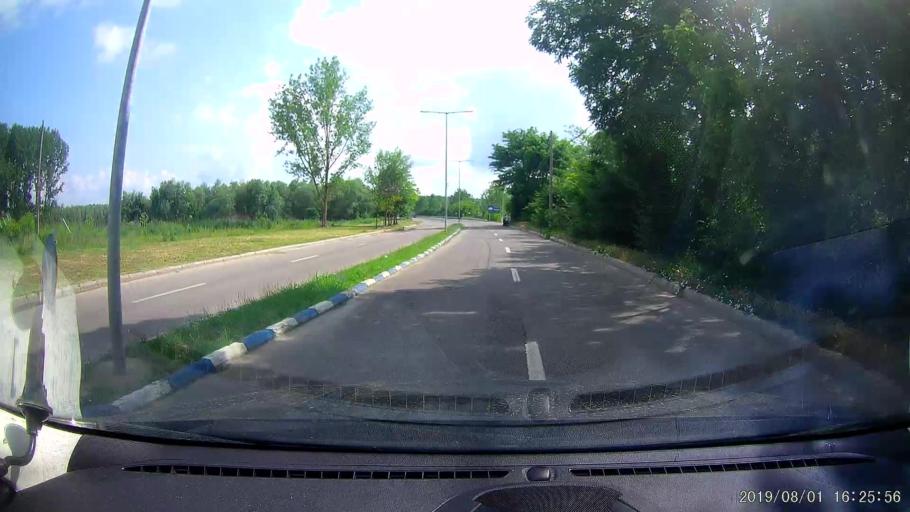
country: RO
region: Calarasi
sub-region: Municipiul Calarasi
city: Calarasi
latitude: 44.1883
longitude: 27.3230
